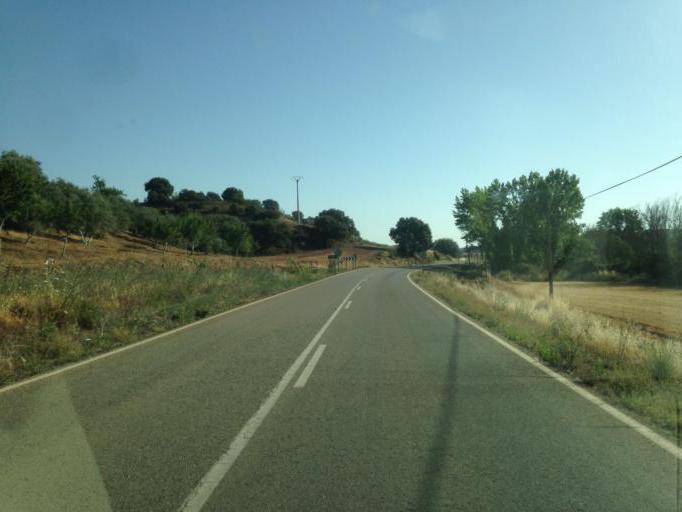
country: ES
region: Andalusia
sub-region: Provincia de Malaga
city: Archidona
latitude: 37.1034
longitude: -4.3590
